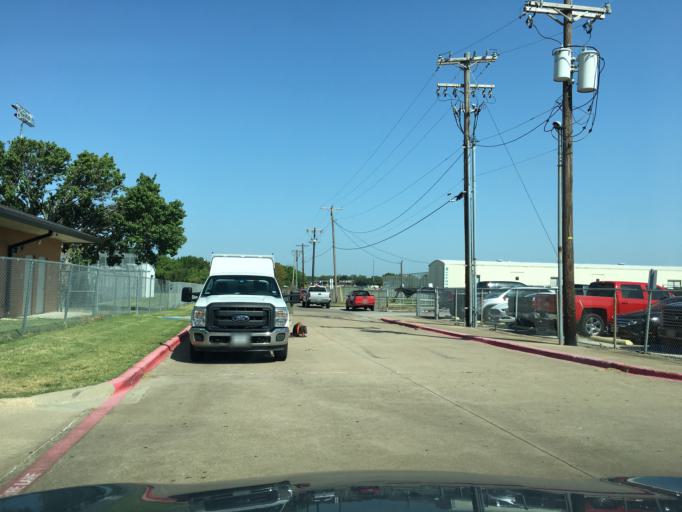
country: US
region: Texas
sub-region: Dallas County
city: Garland
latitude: 32.8727
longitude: -96.6198
